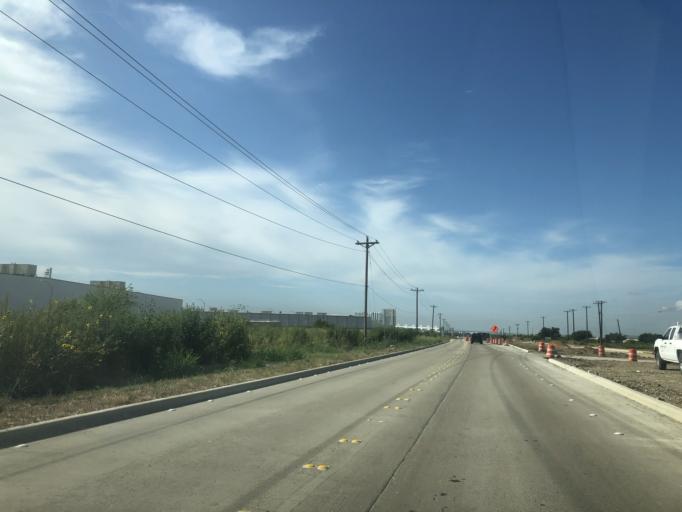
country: US
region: Texas
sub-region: Denton County
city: Justin
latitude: 33.0384
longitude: -97.3065
